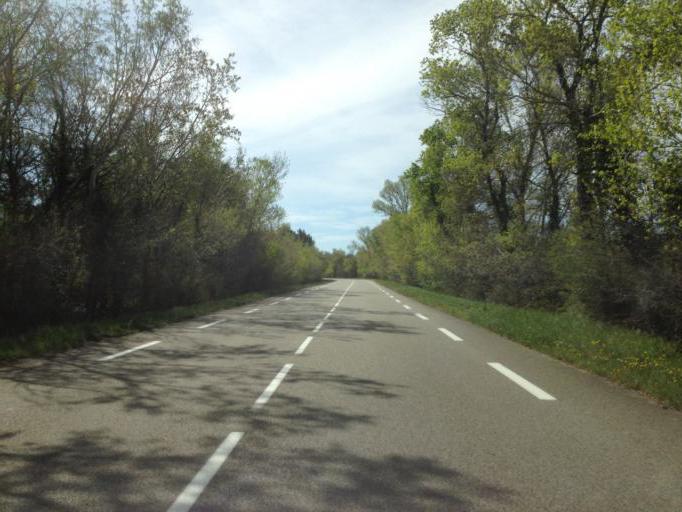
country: FR
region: Provence-Alpes-Cote d'Azur
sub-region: Departement du Vaucluse
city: Caderousse
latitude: 44.1092
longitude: 4.7272
